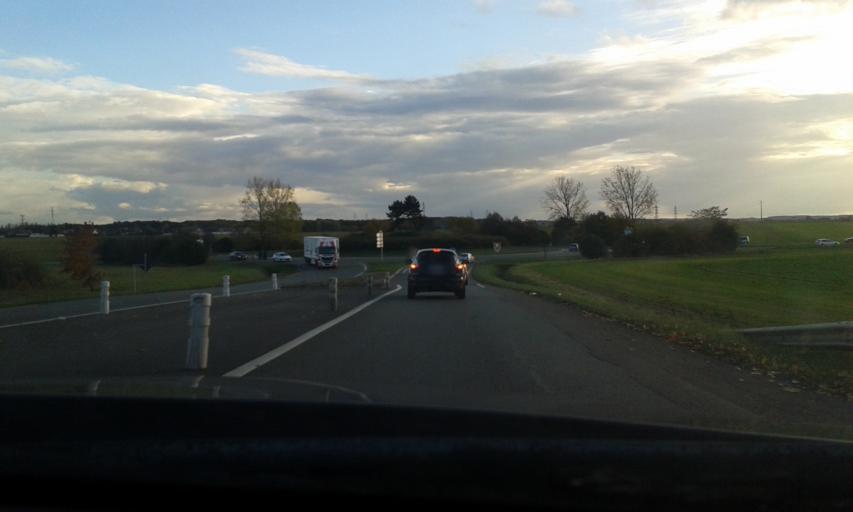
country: FR
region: Centre
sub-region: Departement d'Eure-et-Loir
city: Mainvilliers
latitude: 48.4383
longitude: 1.4309
